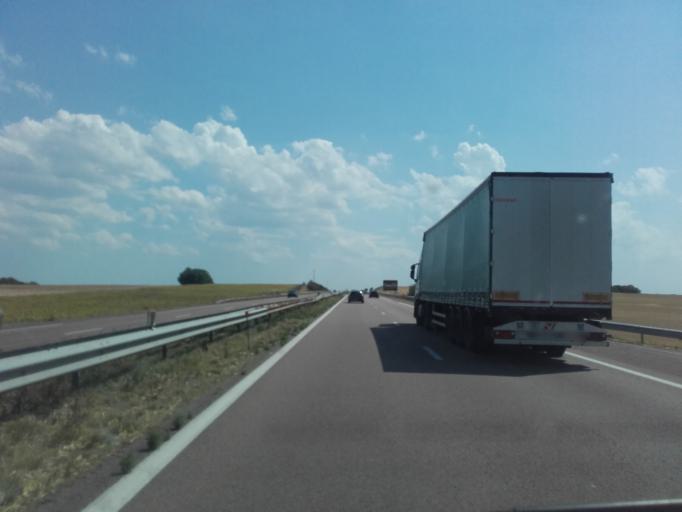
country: FR
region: Bourgogne
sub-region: Departement de l'Yonne
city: Joux-la-Ville
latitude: 47.5708
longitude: 3.9382
